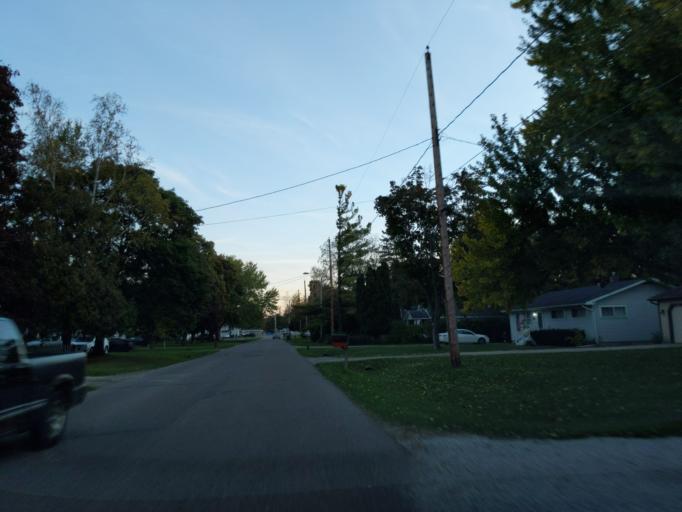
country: US
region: Michigan
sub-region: Ingham County
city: Edgemont Park
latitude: 42.7287
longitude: -84.5981
